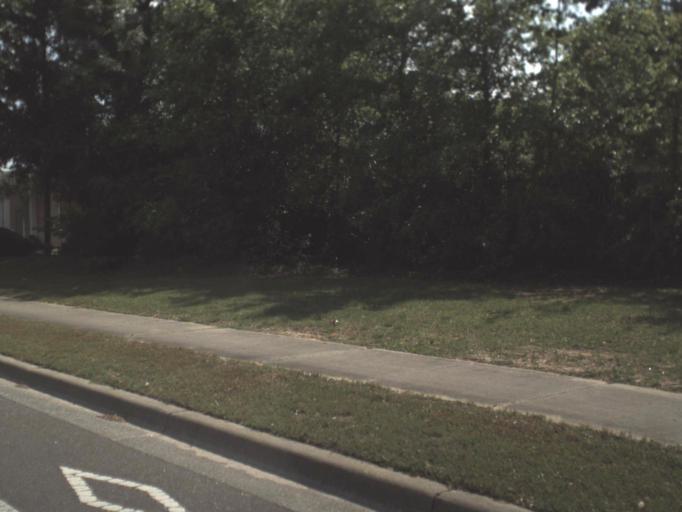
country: US
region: Florida
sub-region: Escambia County
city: Ferry Pass
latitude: 30.5060
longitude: -87.1844
